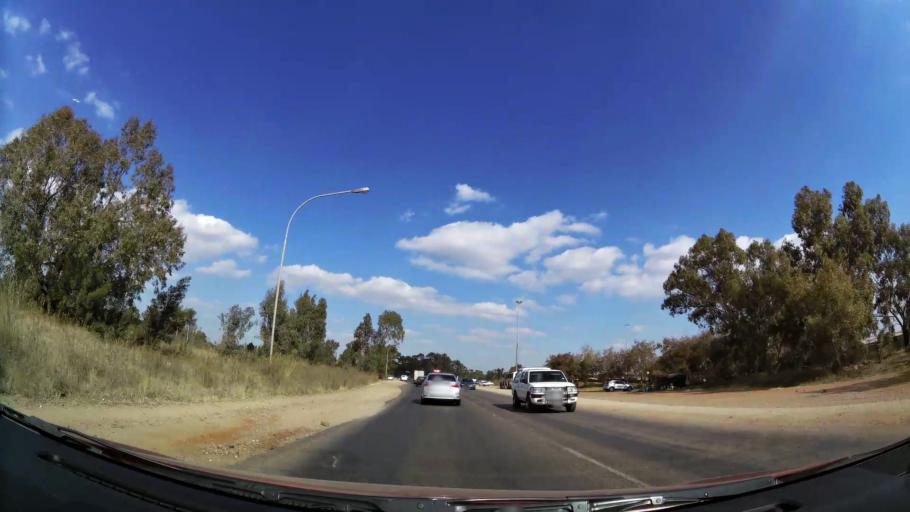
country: ZA
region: Gauteng
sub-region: Ekurhuleni Metropolitan Municipality
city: Tembisa
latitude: -26.0046
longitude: 28.2497
